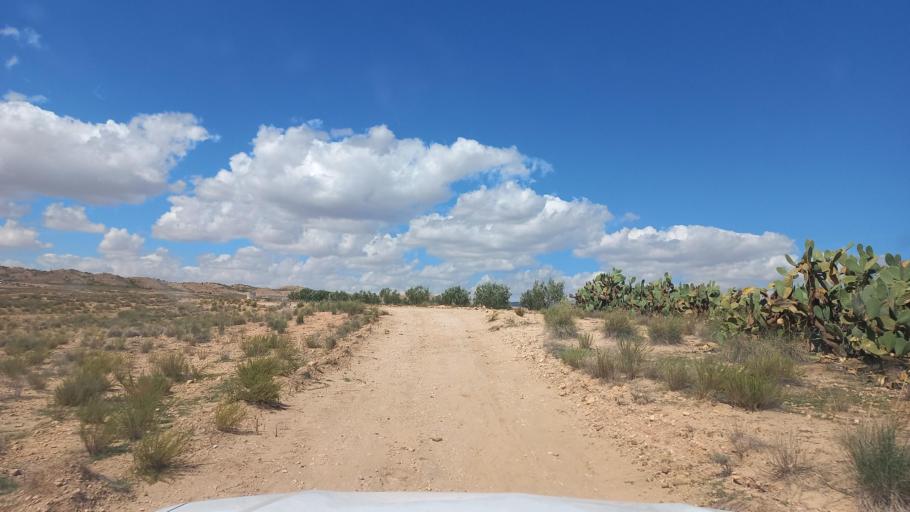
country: TN
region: Al Qasrayn
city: Sbiba
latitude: 35.3542
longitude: 9.0119
